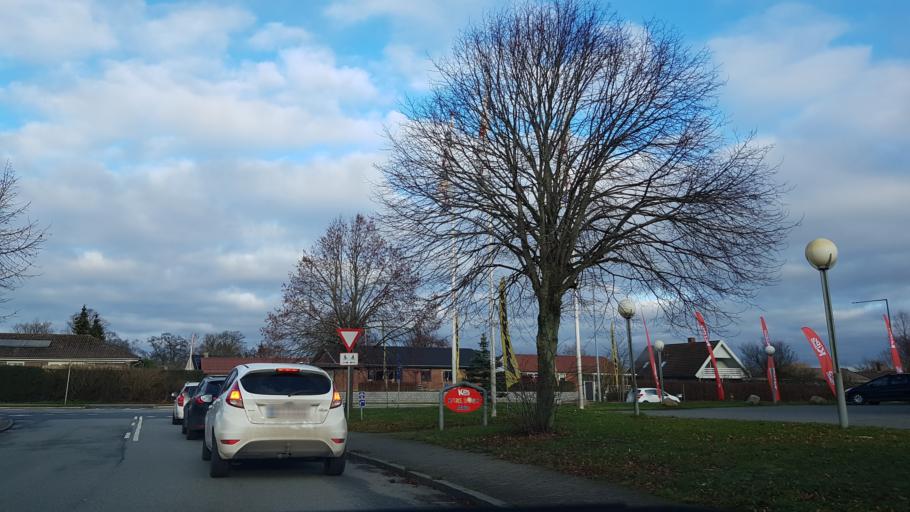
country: DK
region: Zealand
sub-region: Slagelse Kommune
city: Slagelse
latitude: 55.3893
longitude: 11.3294
